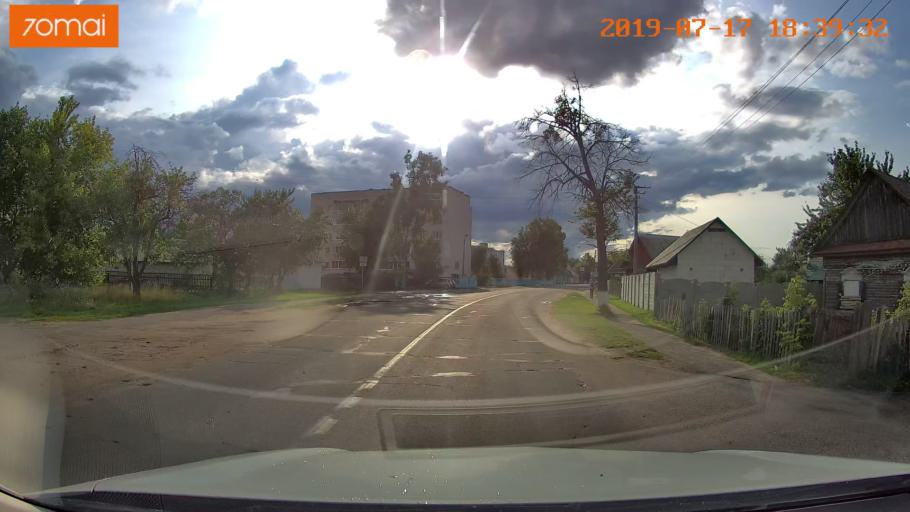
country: BY
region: Mogilev
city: Asipovichy
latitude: 53.2979
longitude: 28.6562
